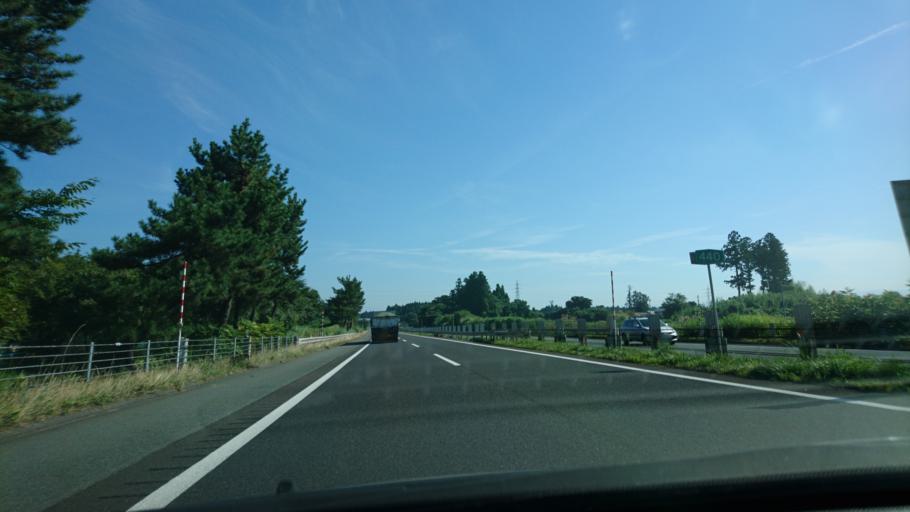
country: JP
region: Iwate
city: Mizusawa
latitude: 39.0904
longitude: 141.1093
